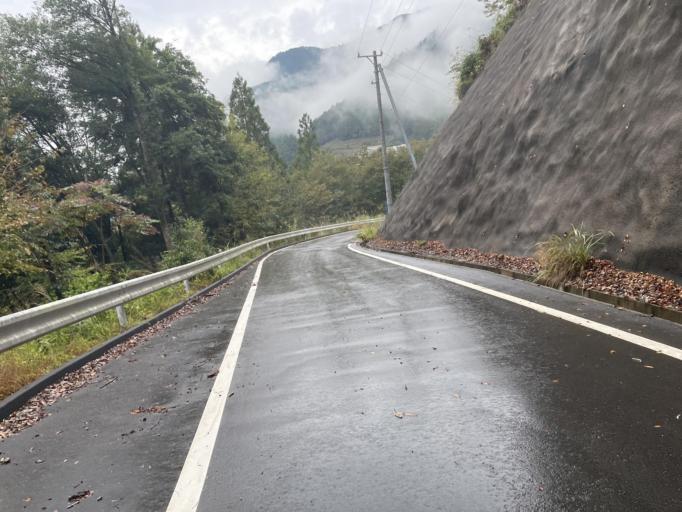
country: JP
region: Nagano
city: Iida
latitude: 35.1901
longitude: 137.8117
